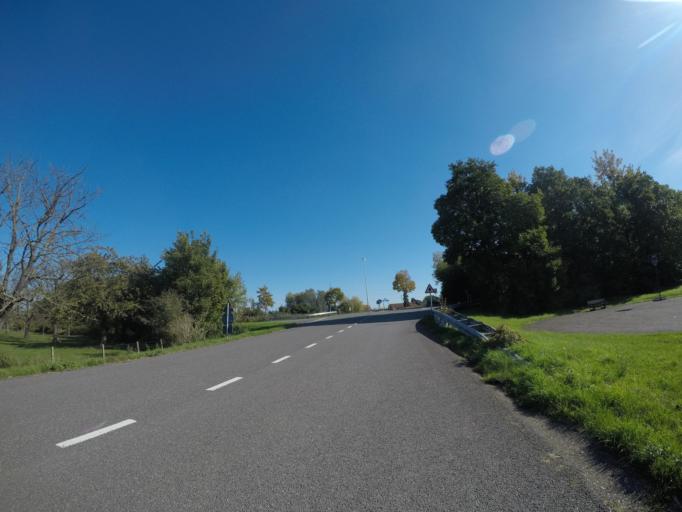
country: BE
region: Flanders
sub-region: Provincie Limburg
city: Alken
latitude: 50.8752
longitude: 5.2830
